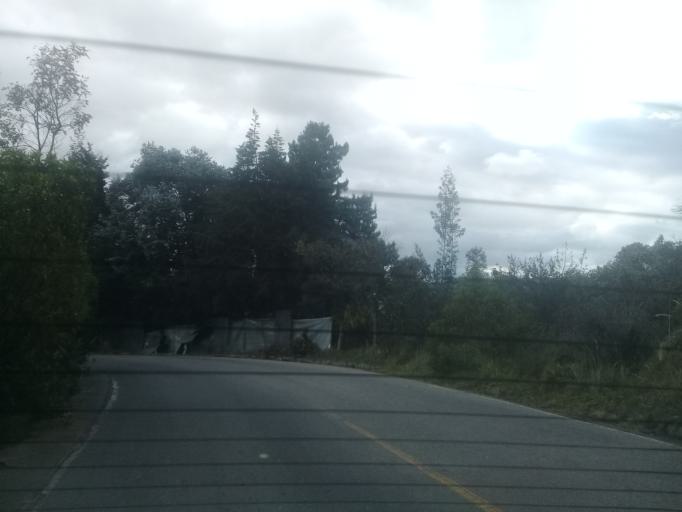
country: CO
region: Cundinamarca
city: Subachoque
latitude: 4.9301
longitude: -74.1561
